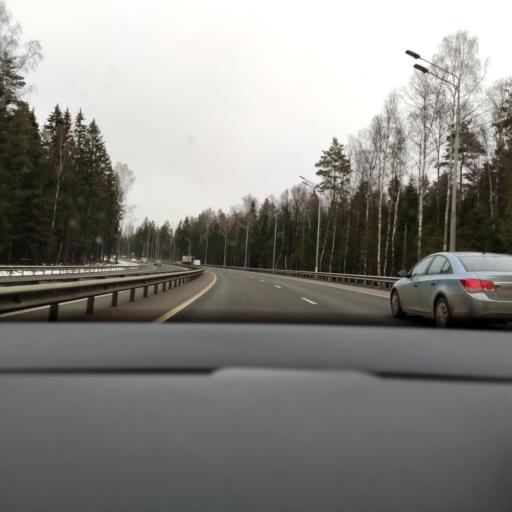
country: RU
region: Moskovskaya
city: Bol'shiye Vyazemy
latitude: 55.6523
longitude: 36.9873
